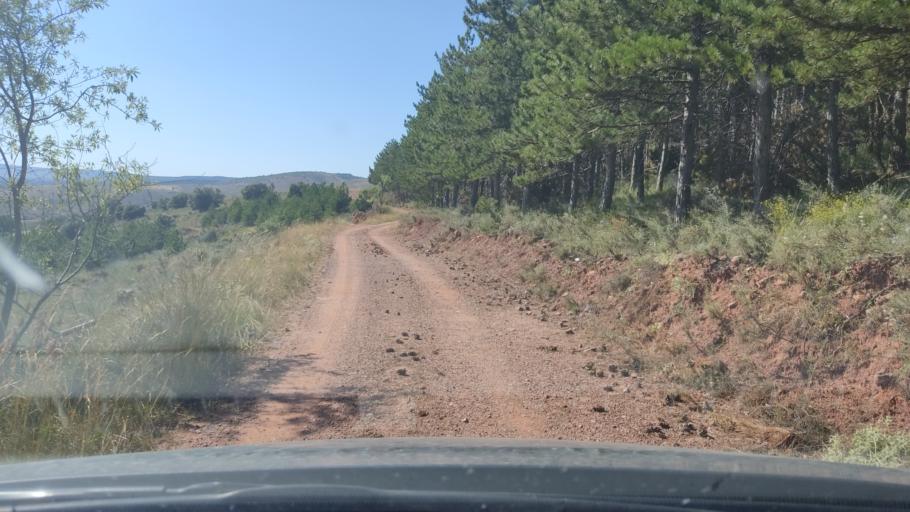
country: ES
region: Aragon
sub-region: Provincia de Teruel
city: Monforte de Moyuela
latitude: 41.0432
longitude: -1.0356
